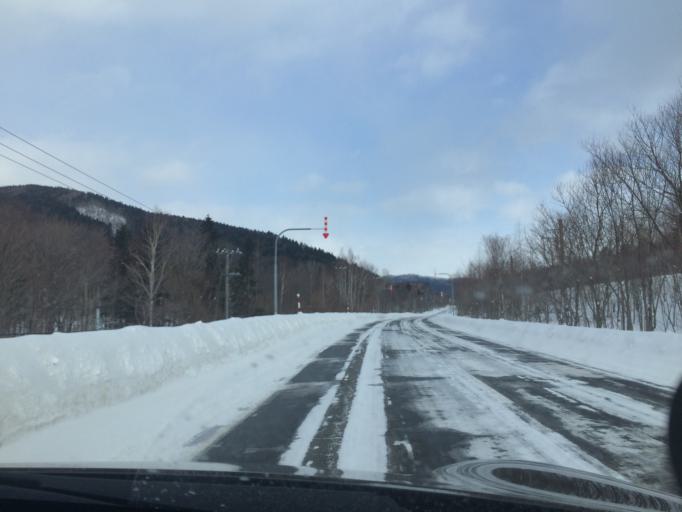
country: JP
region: Hokkaido
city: Shimo-furano
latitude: 43.0556
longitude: 142.5977
